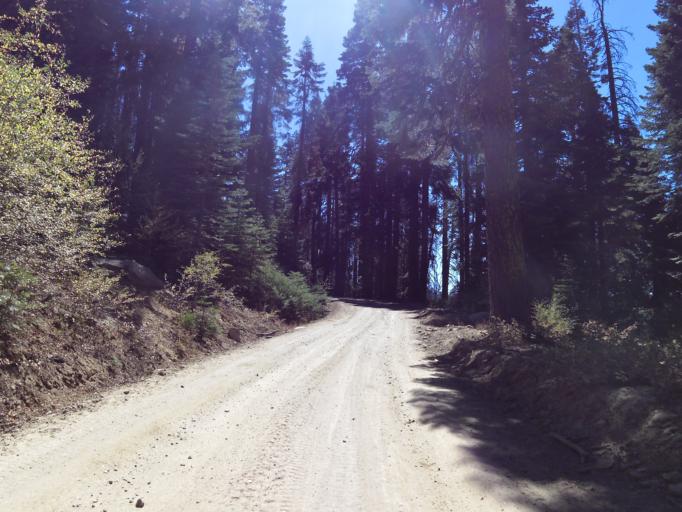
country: US
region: California
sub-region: Madera County
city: Oakhurst
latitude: 37.4382
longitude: -119.5151
